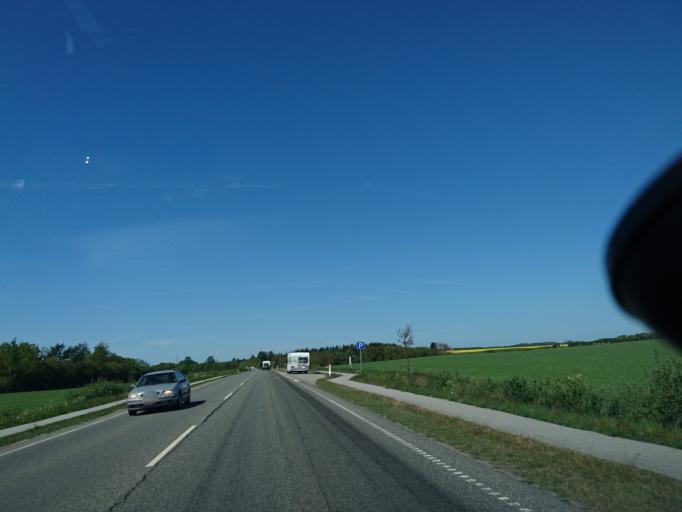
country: DK
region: North Denmark
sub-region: Hjorring Kommune
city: Tars
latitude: 57.4562
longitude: 10.0870
